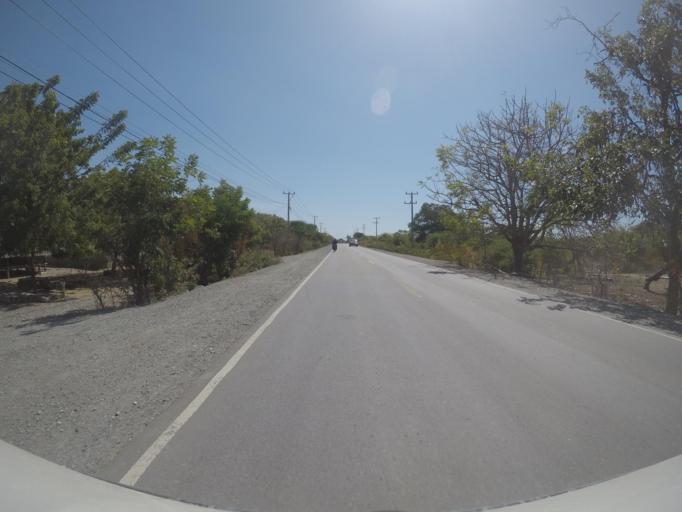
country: TL
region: Liquica
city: Liquica
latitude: -8.5644
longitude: 125.4143
